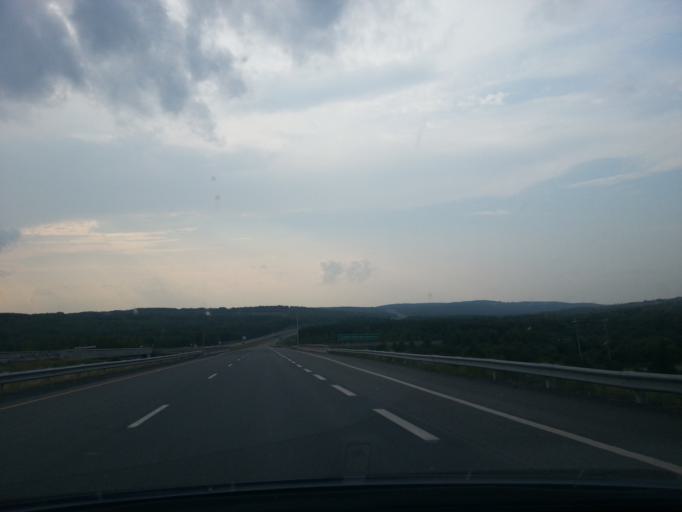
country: CA
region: New Brunswick
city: Harrison Brook
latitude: 47.2265
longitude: -67.9537
